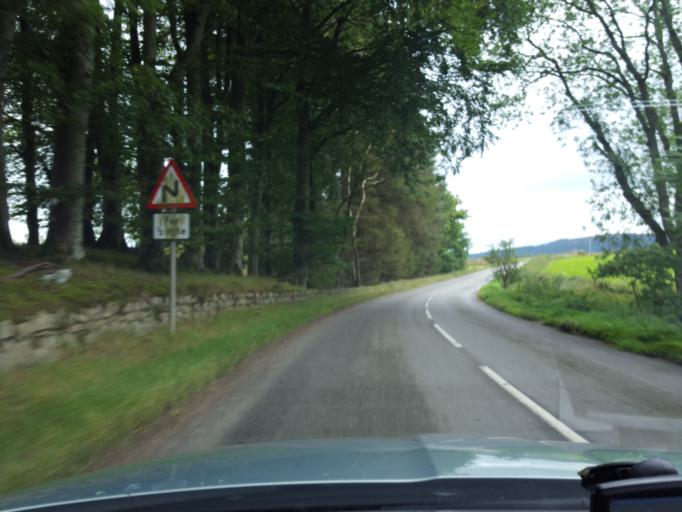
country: GB
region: Scotland
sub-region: Aberdeenshire
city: Kemnay
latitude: 57.1561
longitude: -2.4303
